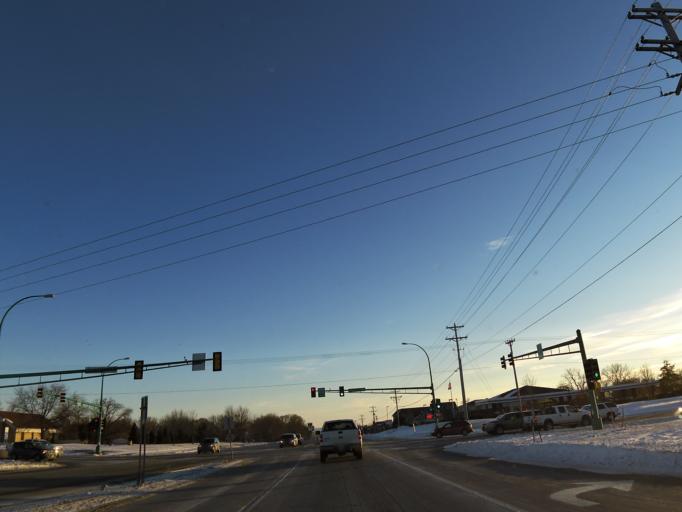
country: US
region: Minnesota
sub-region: Carver County
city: Chaska
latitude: 44.8059
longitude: -93.6020
